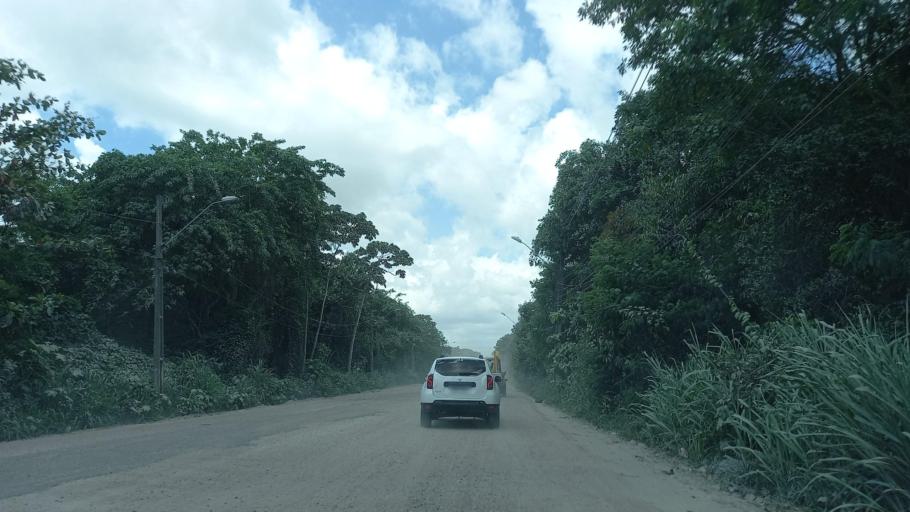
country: BR
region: Pernambuco
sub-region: Jaboatao Dos Guararapes
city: Jaboatao
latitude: -8.1587
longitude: -34.9766
